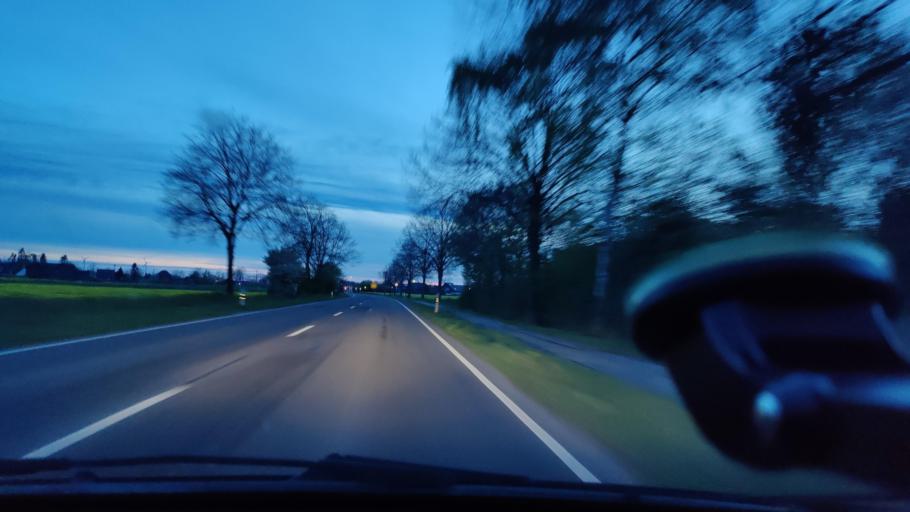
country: DE
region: North Rhine-Westphalia
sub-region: Regierungsbezirk Dusseldorf
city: Alpen
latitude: 51.6282
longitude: 6.4998
